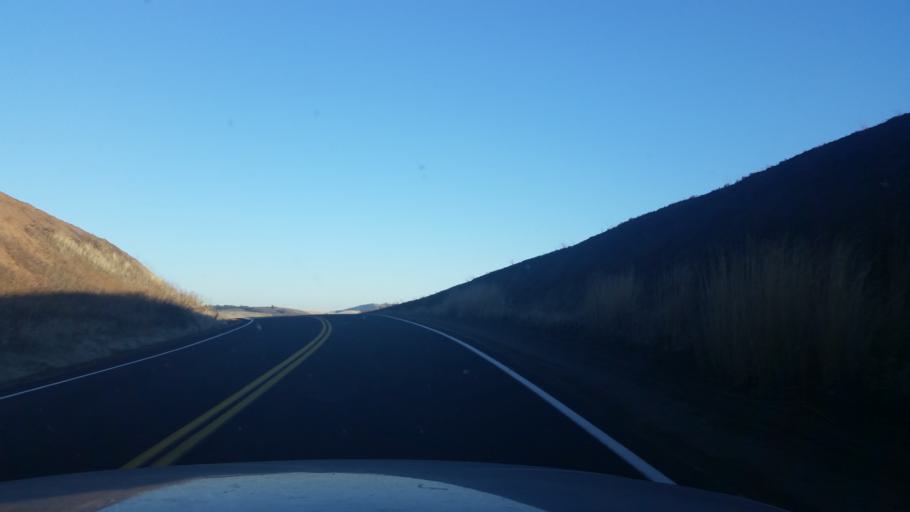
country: US
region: Washington
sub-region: Spokane County
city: Opportunity
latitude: 47.3571
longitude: -117.2721
